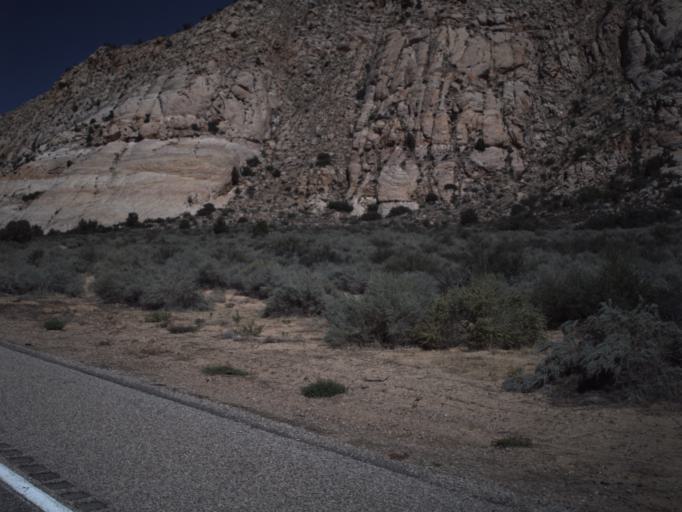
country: US
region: Utah
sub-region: Washington County
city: Ivins
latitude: 37.2322
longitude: -113.6340
